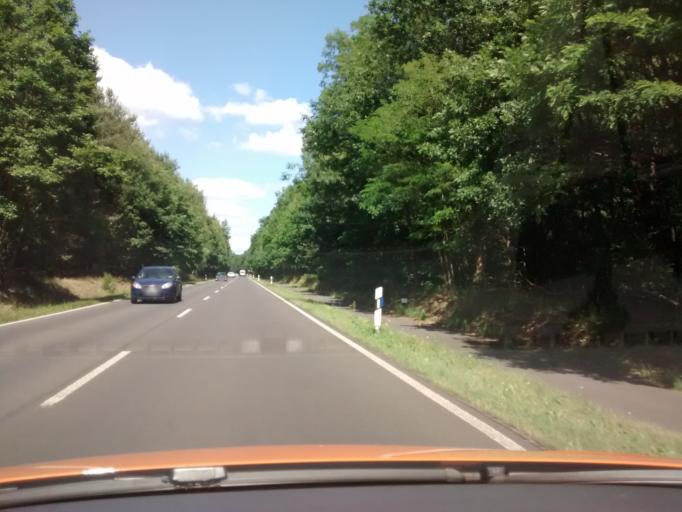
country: DE
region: Berlin
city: Kladow
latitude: 52.4911
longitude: 13.1190
